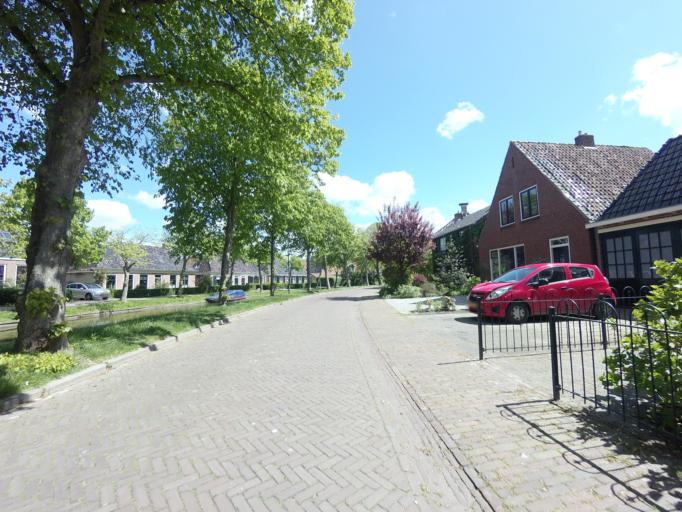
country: NL
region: Friesland
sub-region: Gemeente Harlingen
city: Harlingen
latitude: 53.1497
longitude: 5.4833
